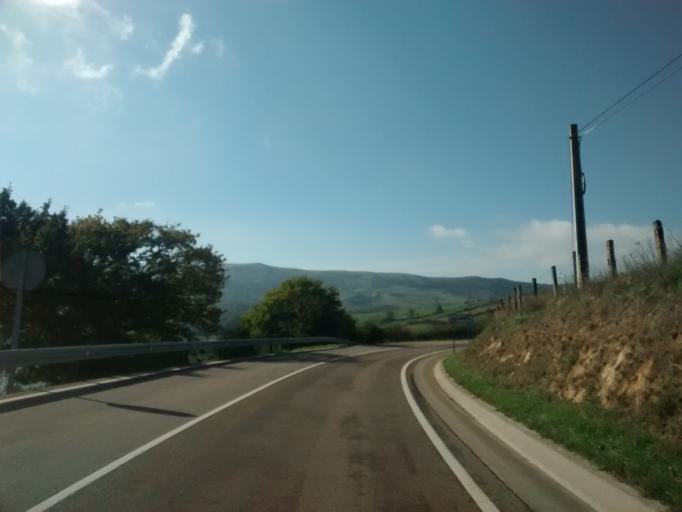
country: ES
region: Cantabria
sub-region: Provincia de Cantabria
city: Reinosa
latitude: 42.9878
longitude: -4.1044
